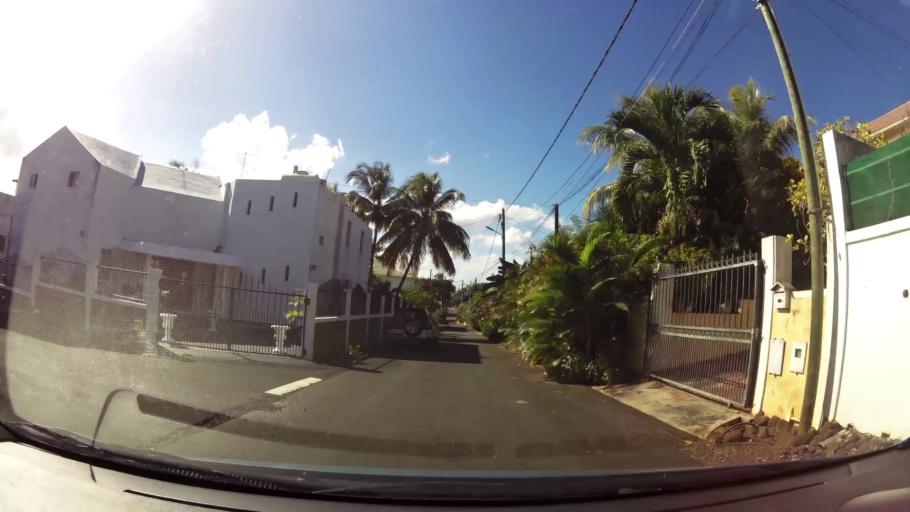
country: MU
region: Black River
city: Albion
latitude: -20.2183
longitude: 57.4053
